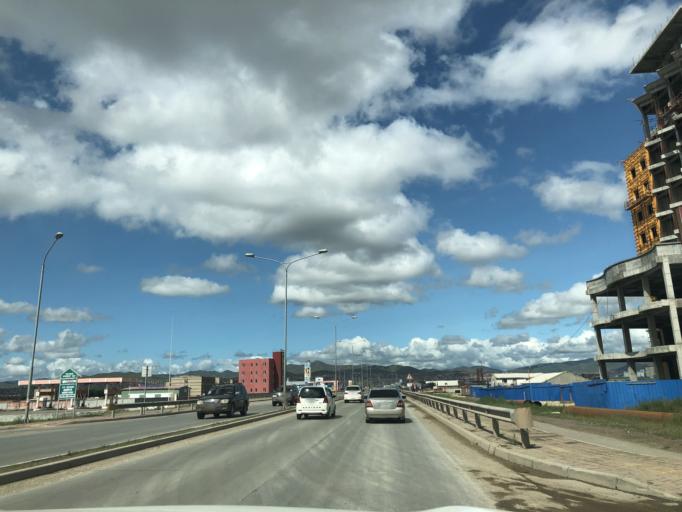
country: MN
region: Ulaanbaatar
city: Ulaanbaatar
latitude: 47.8912
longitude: 106.7854
